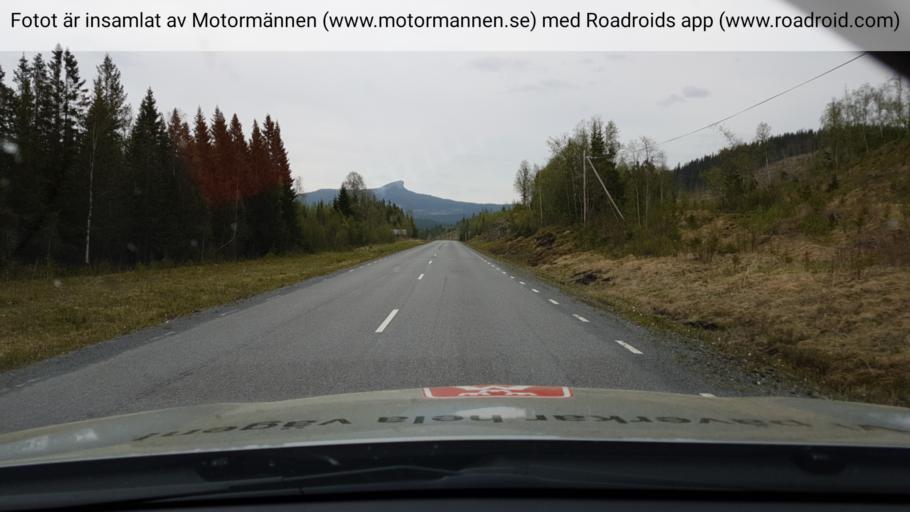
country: SE
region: Jaemtland
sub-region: Are Kommun
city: Are
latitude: 63.5889
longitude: 13.0432
